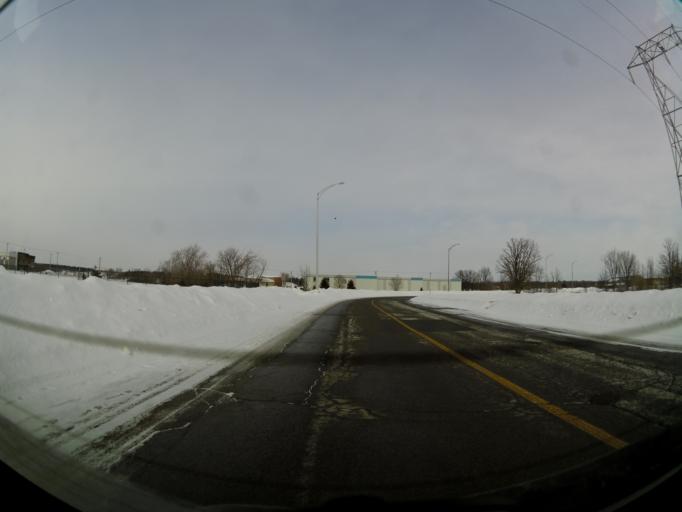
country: CA
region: Quebec
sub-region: Outaouais
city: Gatineau
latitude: 45.5159
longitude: -75.5627
